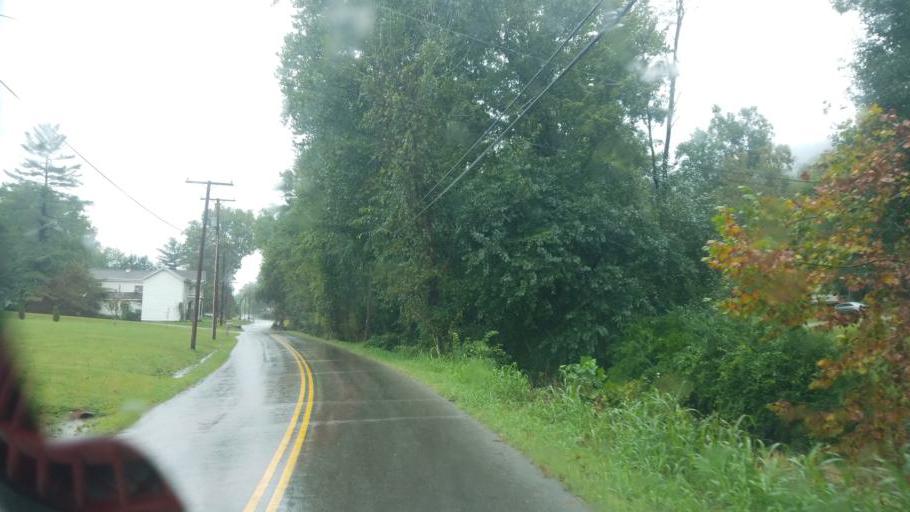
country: US
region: Ohio
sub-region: Scioto County
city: West Portsmouth
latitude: 38.7274
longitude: -83.0517
